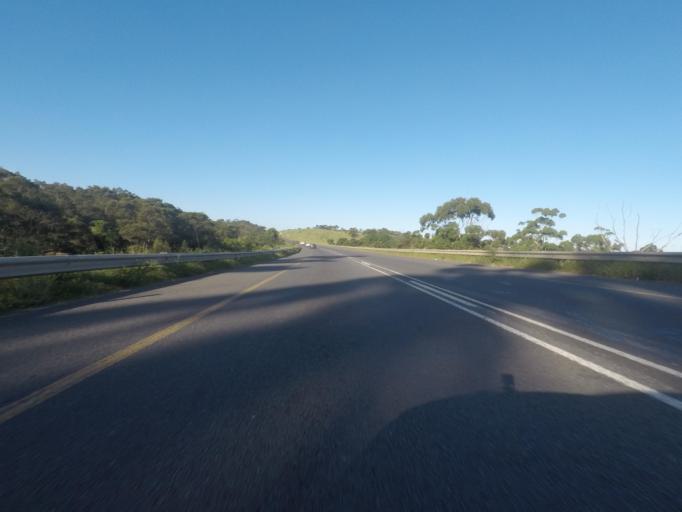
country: ZA
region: Eastern Cape
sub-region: Buffalo City Metropolitan Municipality
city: East London
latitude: -33.0442
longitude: 27.8275
